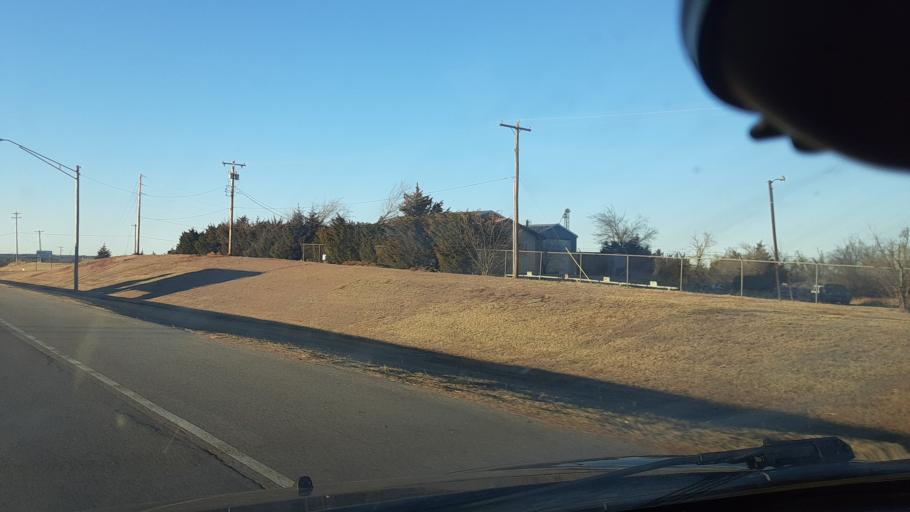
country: US
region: Oklahoma
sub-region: Logan County
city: Guthrie
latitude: 35.8255
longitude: -97.4214
